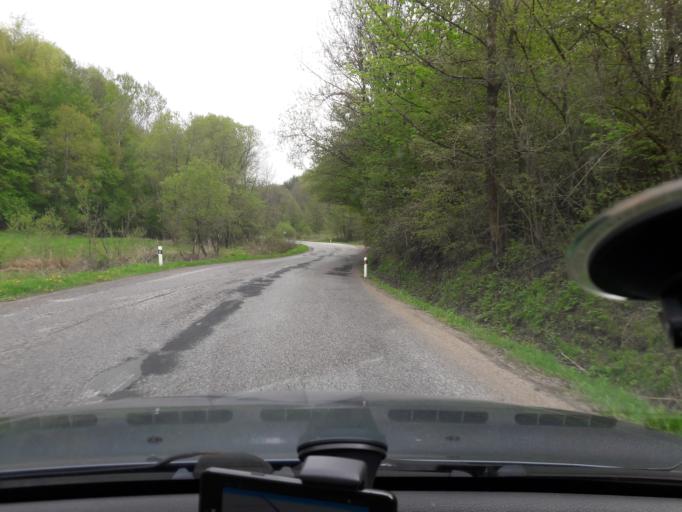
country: SK
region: Banskobystricky
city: Tisovec
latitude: 48.7099
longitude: 19.9973
